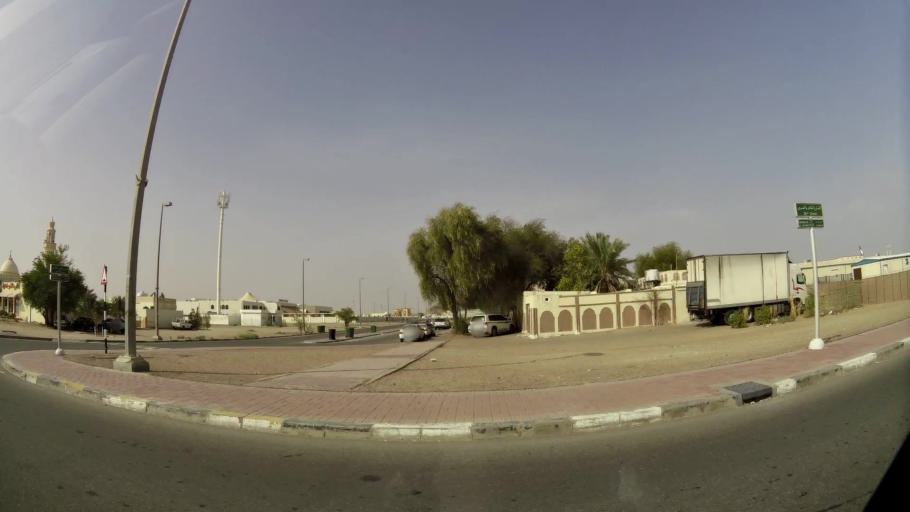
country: AE
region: Abu Dhabi
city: Al Ain
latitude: 24.2103
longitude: 55.5865
